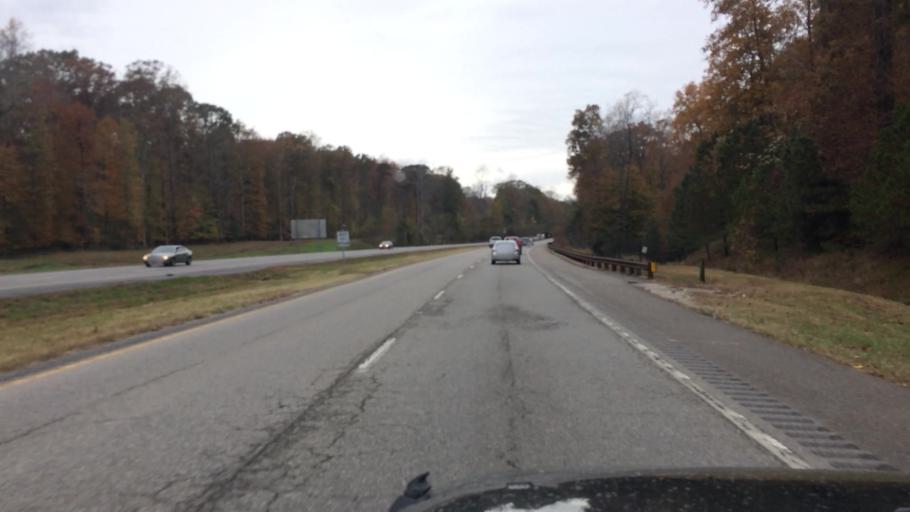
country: US
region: Virginia
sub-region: City of Williamsburg
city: Williamsburg
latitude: 37.2476
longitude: -76.6736
